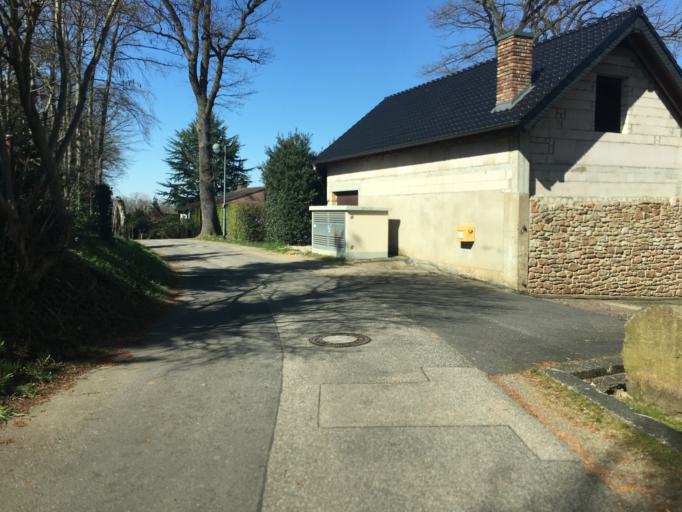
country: DE
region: North Rhine-Westphalia
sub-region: Regierungsbezirk Koln
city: Kreuzau
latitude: 50.7409
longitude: 6.4561
